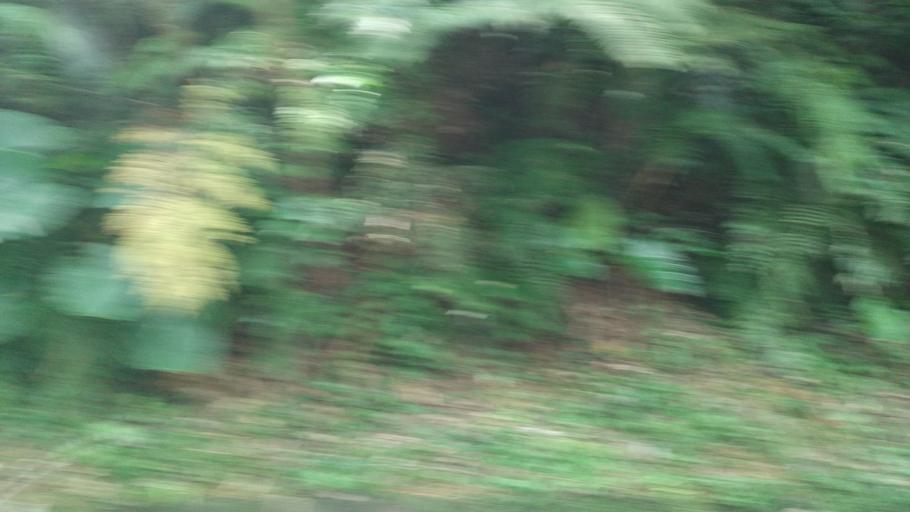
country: TW
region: Taiwan
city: Daxi
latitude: 24.9114
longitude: 121.3954
